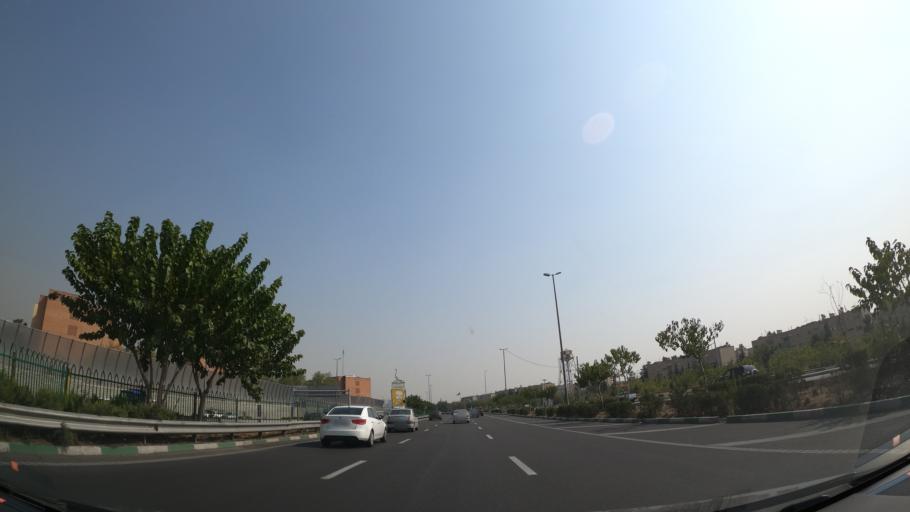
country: IR
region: Tehran
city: Shahr-e Qods
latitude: 35.7585
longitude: 51.2590
